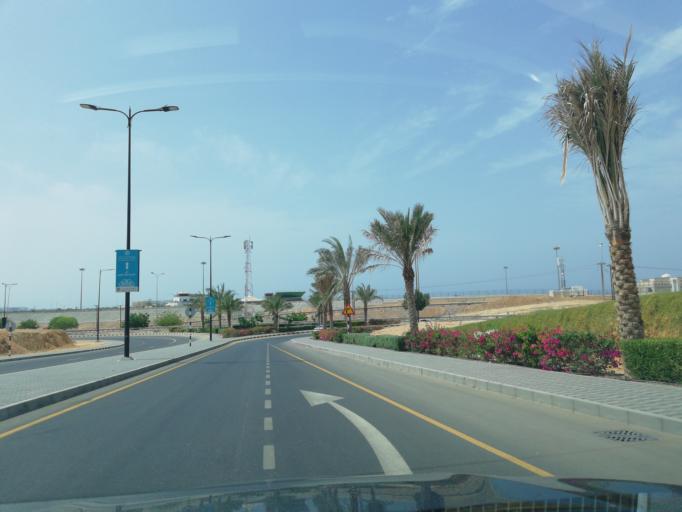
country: OM
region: Muhafazat Masqat
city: Bawshar
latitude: 23.5803
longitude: 58.3219
